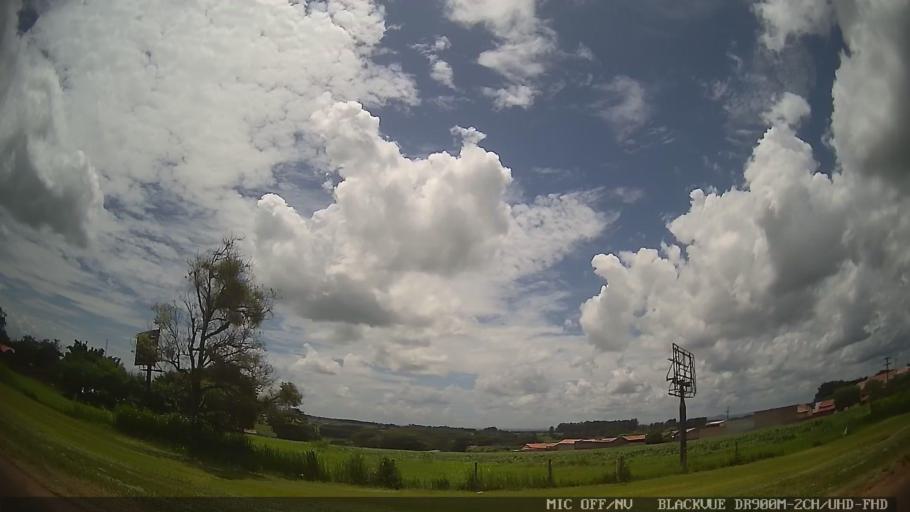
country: BR
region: Sao Paulo
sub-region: Laranjal Paulista
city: Laranjal Paulista
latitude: -23.0366
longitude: -47.8853
